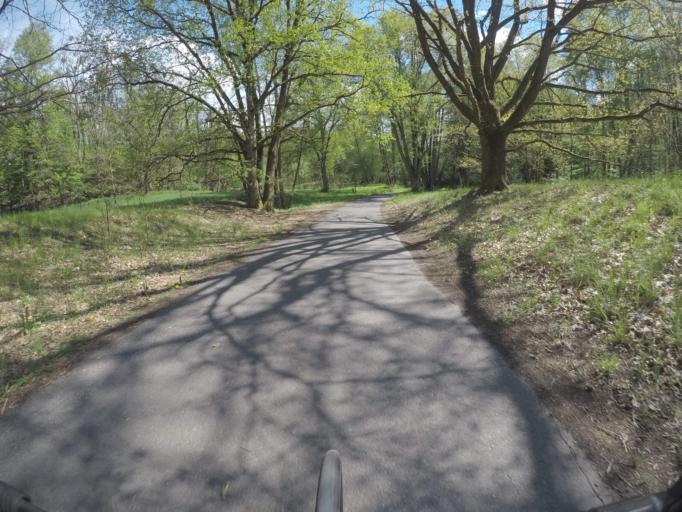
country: DE
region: Brandenburg
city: Rudnitz
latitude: 52.7414
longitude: 13.6147
